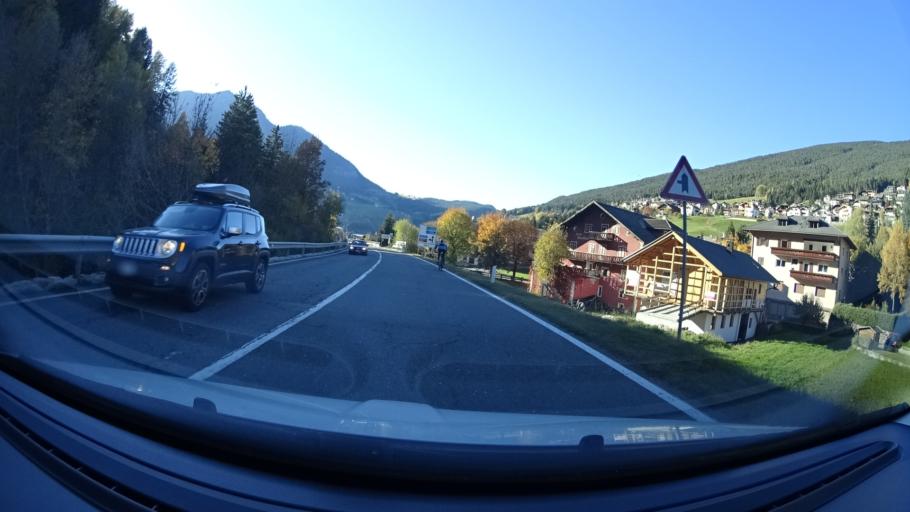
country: IT
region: Trentino-Alto Adige
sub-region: Bolzano
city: Ortisei
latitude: 46.5736
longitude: 11.6630
